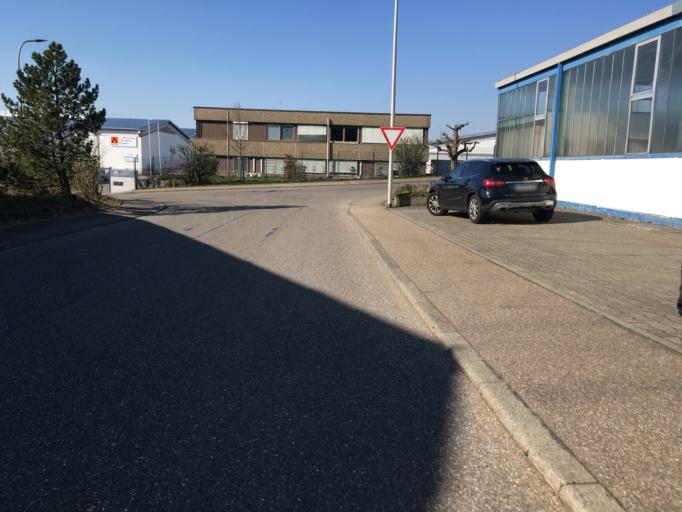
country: DE
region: Baden-Wuerttemberg
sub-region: Regierungsbezirk Stuttgart
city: Talheim
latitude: 49.0974
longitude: 9.1875
